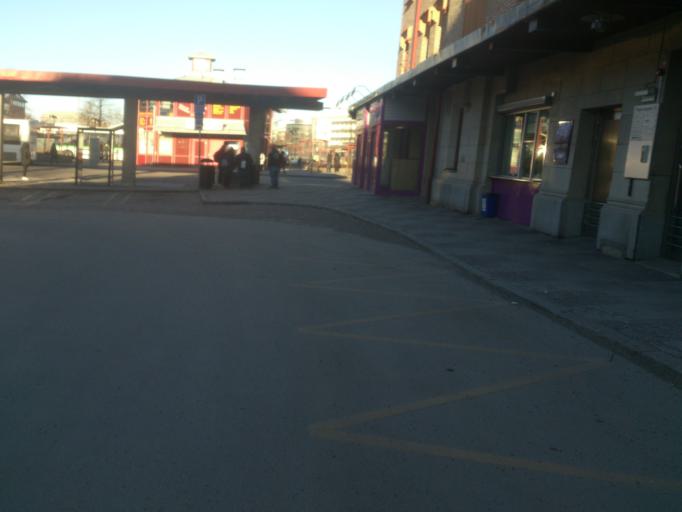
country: SE
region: Vaesternorrland
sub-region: Sundsvalls Kommun
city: Sundsvall
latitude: 62.3921
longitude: 17.3102
